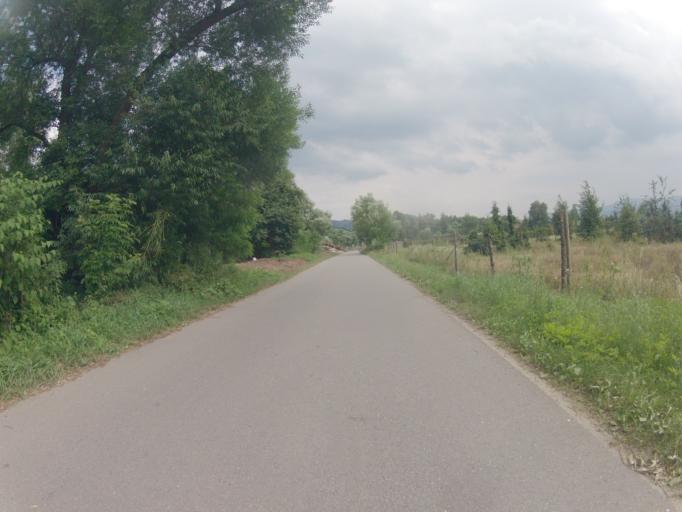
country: PL
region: Lesser Poland Voivodeship
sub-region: Powiat nowosadecki
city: Stary Sacz
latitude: 49.5605
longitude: 20.6598
